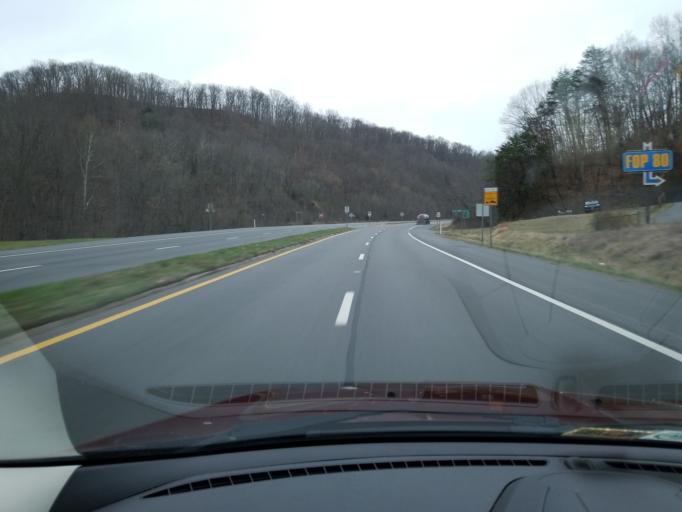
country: US
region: Virginia
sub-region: Giles County
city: Narrows
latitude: 37.3669
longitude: -80.8688
